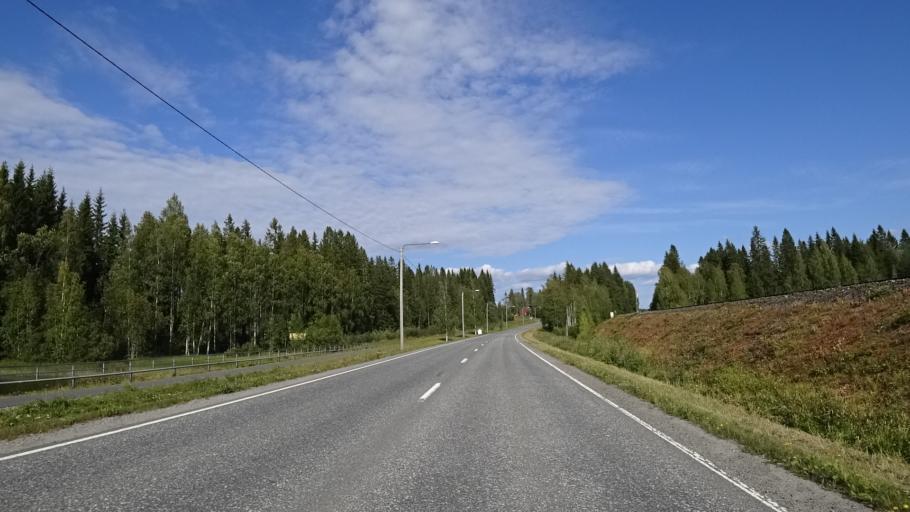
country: FI
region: North Karelia
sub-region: Joensuu
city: Eno
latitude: 62.8038
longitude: 30.1238
